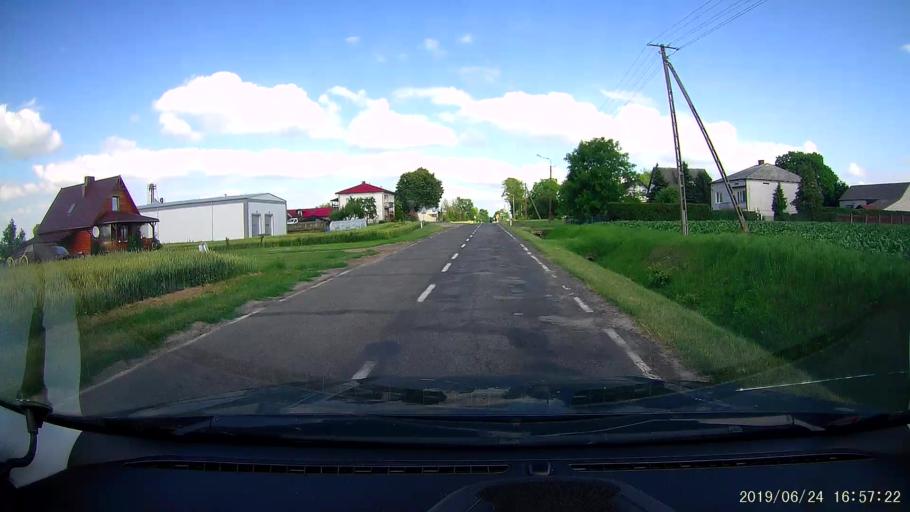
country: PL
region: Lublin Voivodeship
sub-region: Powiat tomaszowski
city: Telatyn
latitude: 50.5263
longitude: 23.8594
